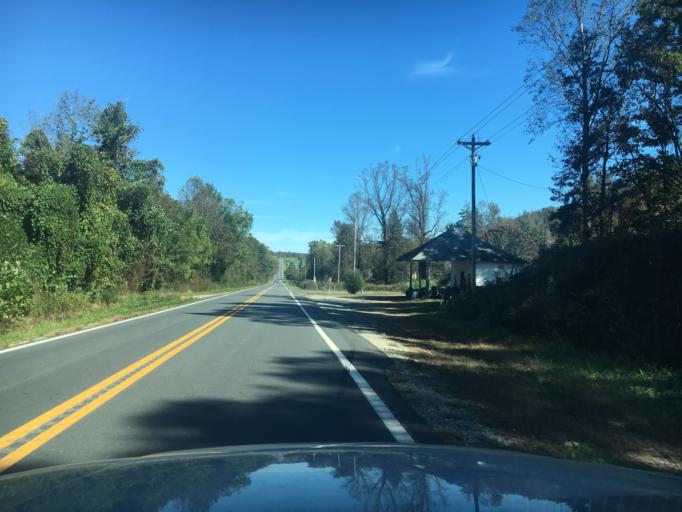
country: US
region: North Carolina
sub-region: Burke County
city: Glen Alpine
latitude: 35.6255
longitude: -81.8027
